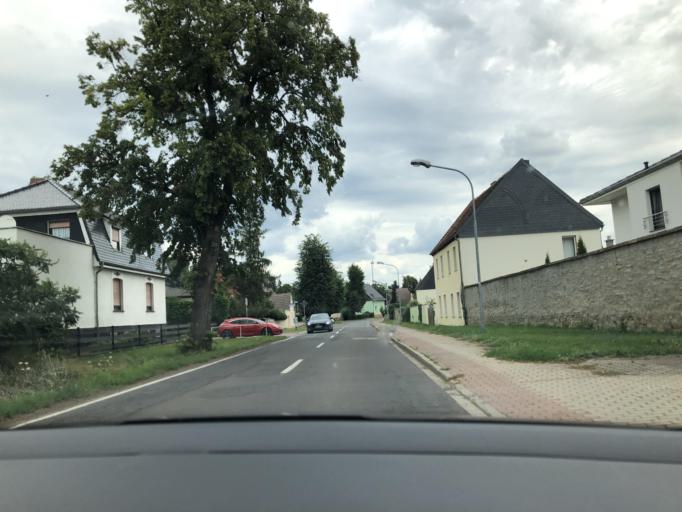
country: DE
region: Saxony-Anhalt
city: Borne
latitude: 51.9473
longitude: 11.5532
